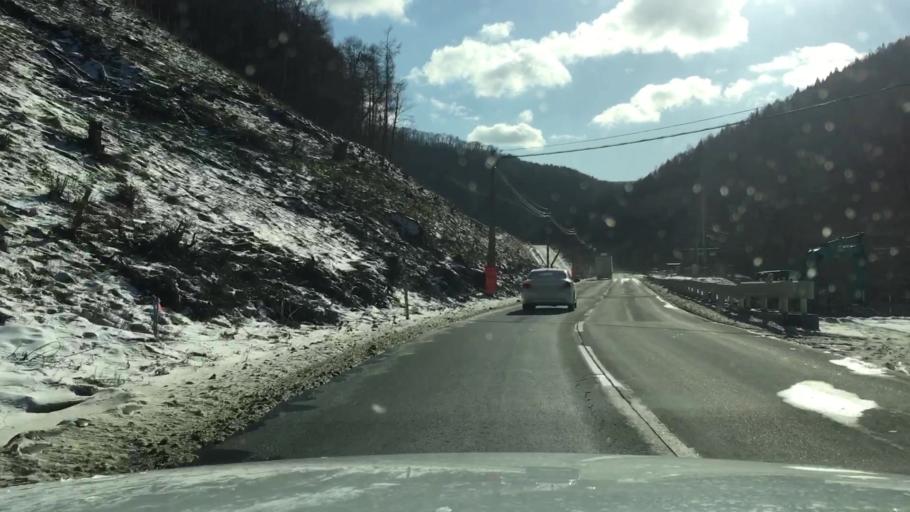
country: JP
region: Iwate
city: Tono
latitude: 39.6258
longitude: 141.4690
